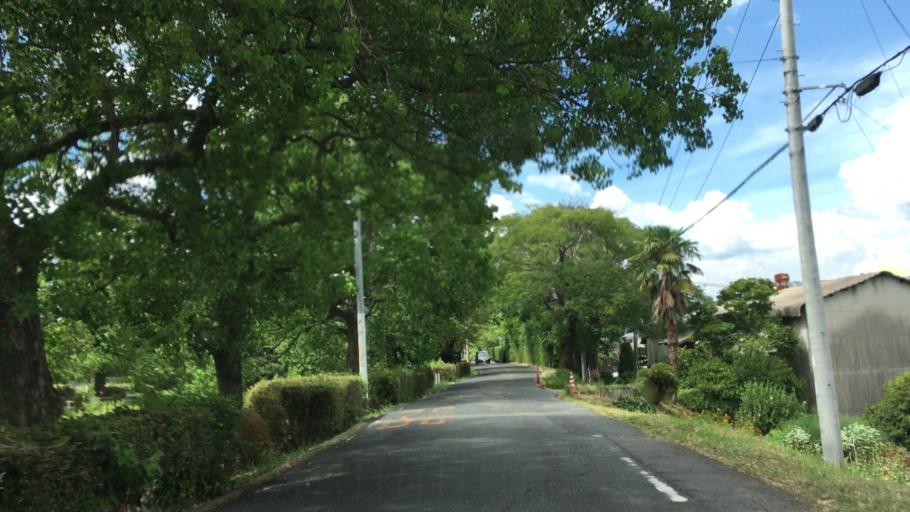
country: JP
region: Saga Prefecture
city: Saga-shi
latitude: 33.2695
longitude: 130.2828
